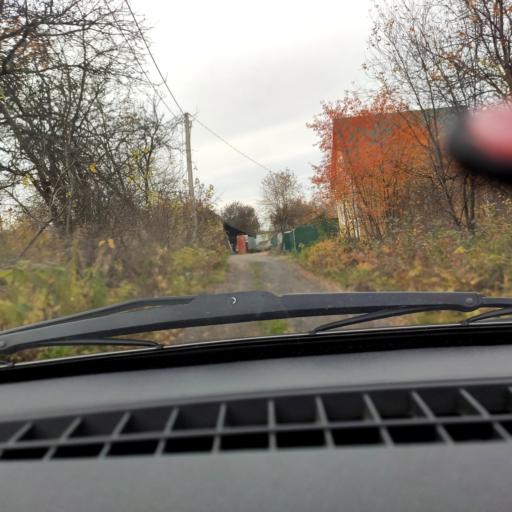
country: RU
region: Bashkortostan
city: Ufa
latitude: 54.8295
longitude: 56.0988
